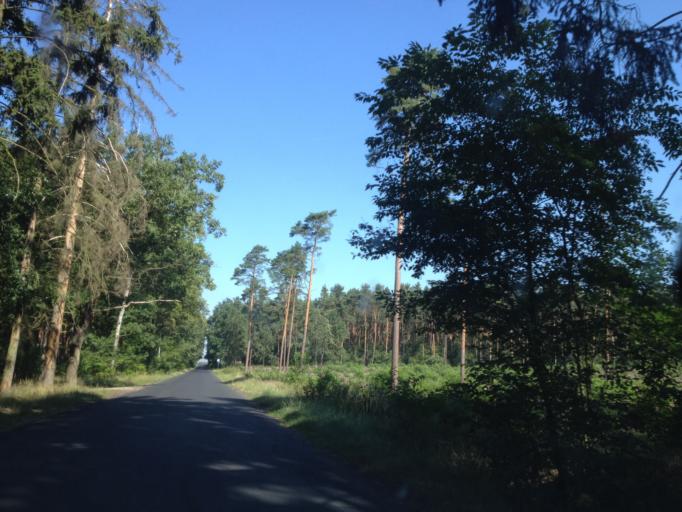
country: PL
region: Greater Poland Voivodeship
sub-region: Powiat sredzki
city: Zaniemysl
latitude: 52.1323
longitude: 17.1016
